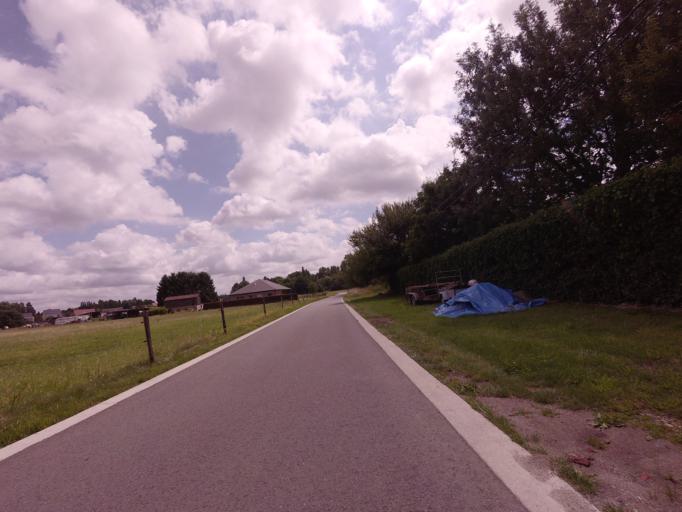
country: BE
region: Flanders
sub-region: Provincie Antwerpen
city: Sint-Katelijne-Waver
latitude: 51.0491
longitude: 4.5134
